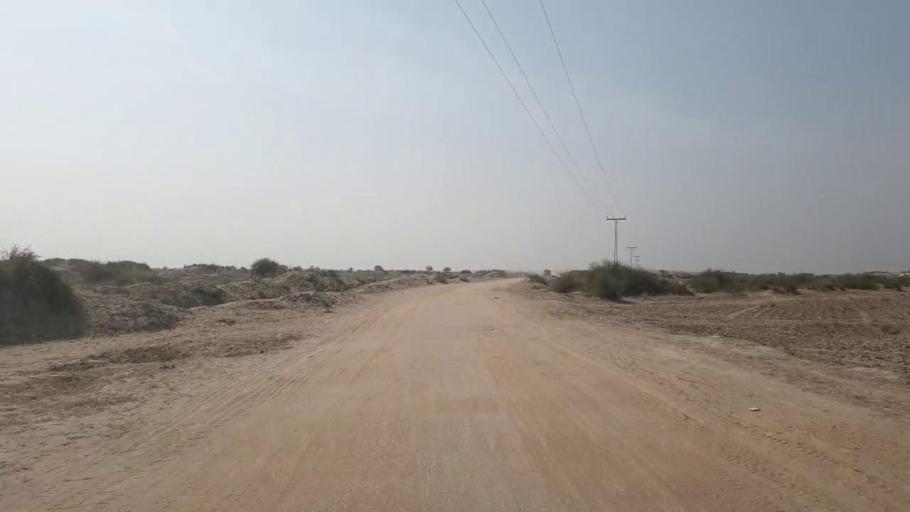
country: PK
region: Sindh
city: Umarkot
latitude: 25.3197
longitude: 69.7302
